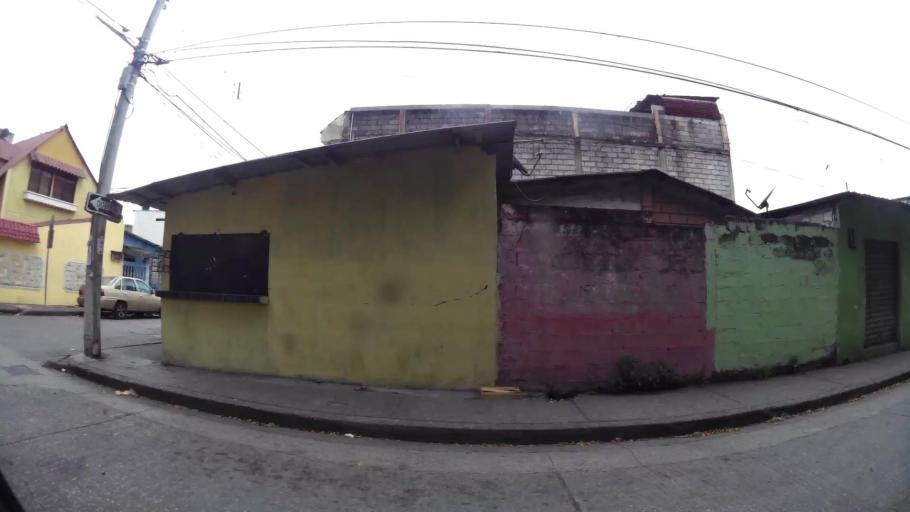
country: EC
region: Guayas
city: Eloy Alfaro
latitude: -2.1223
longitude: -79.8887
